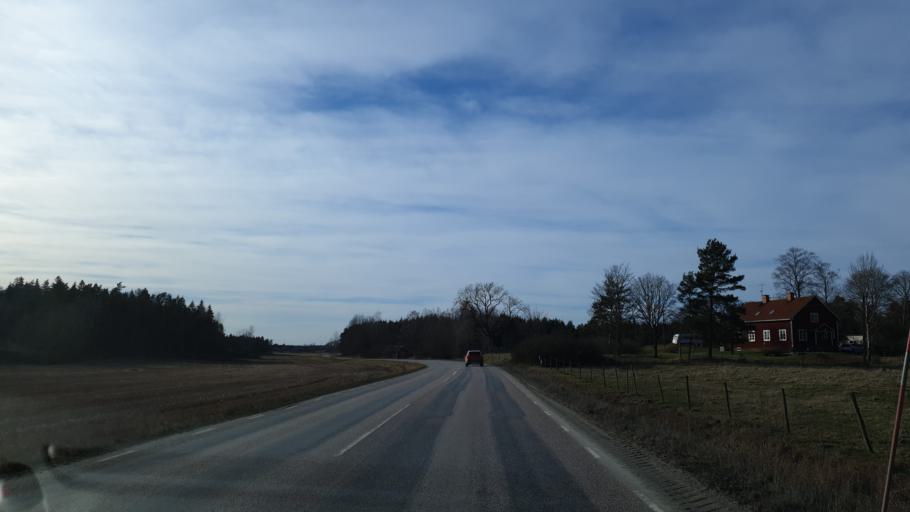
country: SE
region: Uppsala
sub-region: Enkopings Kommun
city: Grillby
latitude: 59.5961
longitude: 17.1743
